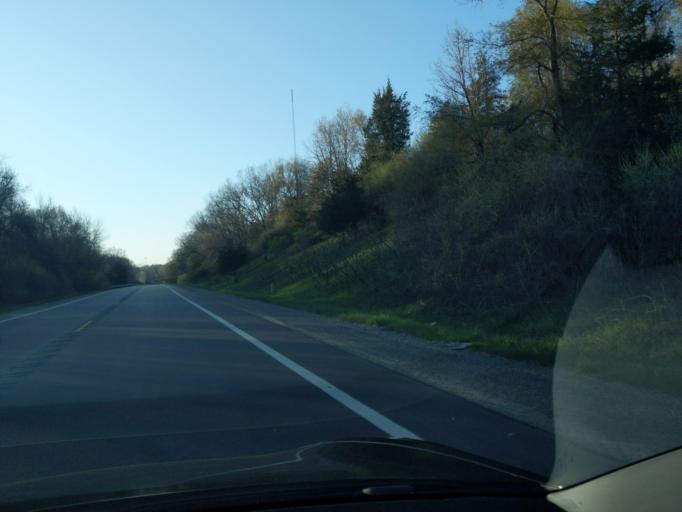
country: US
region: Michigan
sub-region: Washtenaw County
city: Chelsea
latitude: 42.3653
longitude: -84.0656
